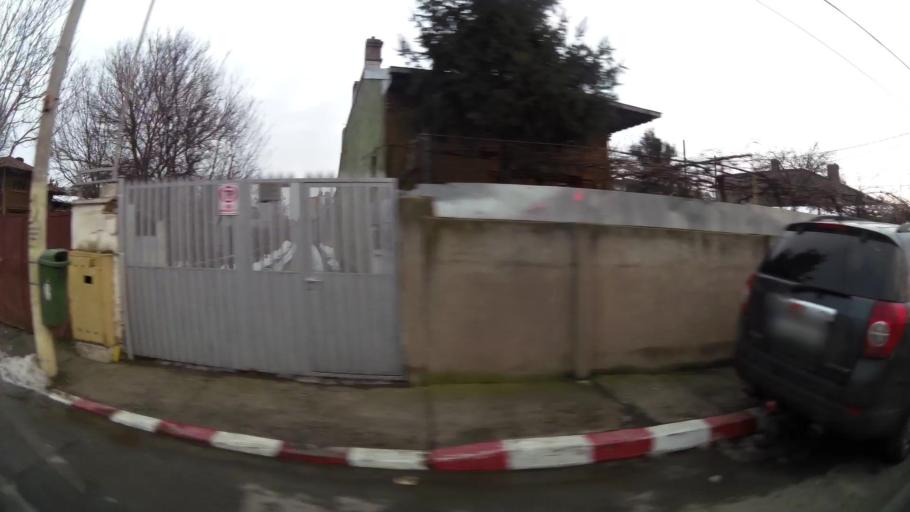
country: RO
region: Ilfov
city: Dobroesti
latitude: 44.4517
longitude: 26.1808
